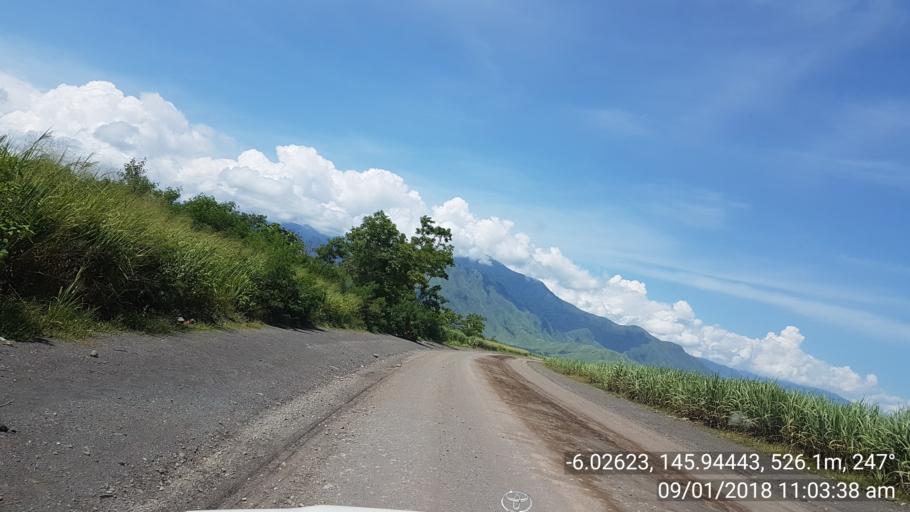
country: PG
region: Eastern Highlands
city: Kainantu
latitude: -6.0262
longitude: 145.9451
